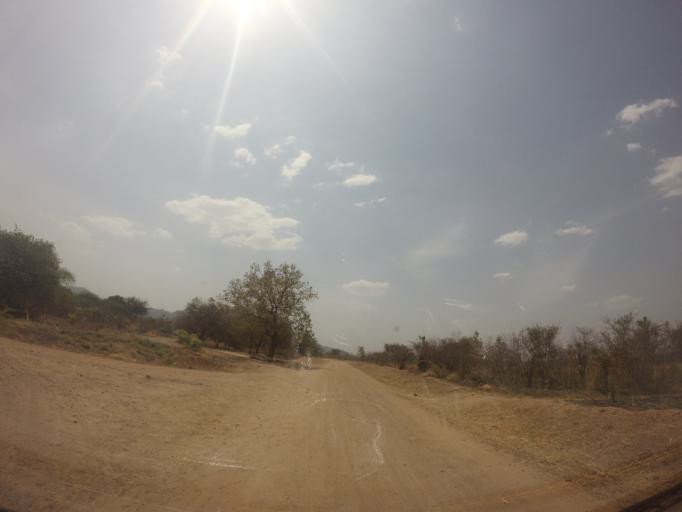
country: UG
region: Northern Region
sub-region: Arua District
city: Arua
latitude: 2.8971
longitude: 31.1261
